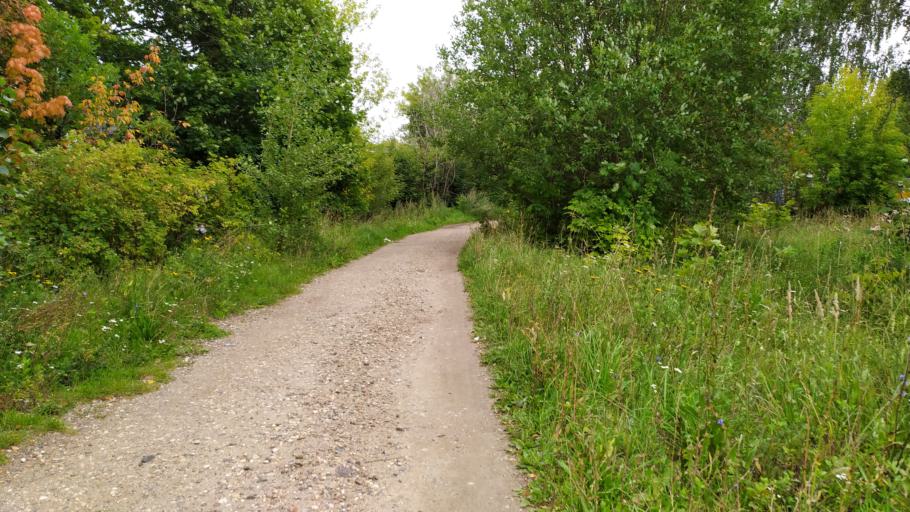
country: RU
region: Ivanovo
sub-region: Gorod Ivanovo
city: Ivanovo
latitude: 56.9761
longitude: 40.9625
